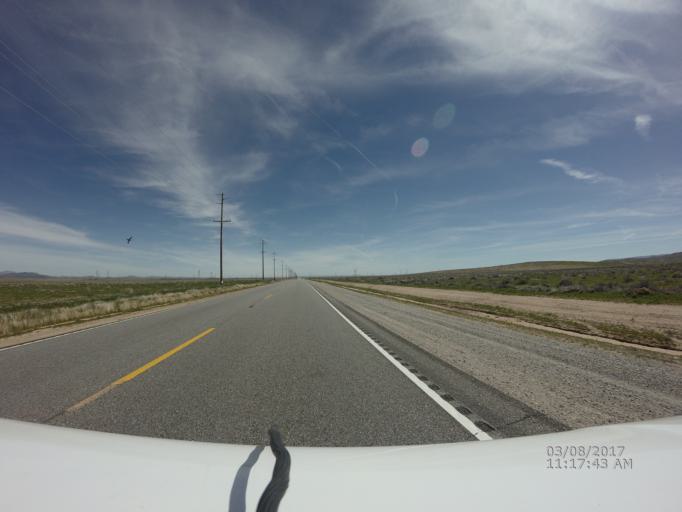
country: US
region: California
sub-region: Los Angeles County
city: Green Valley
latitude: 34.7755
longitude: -118.3938
